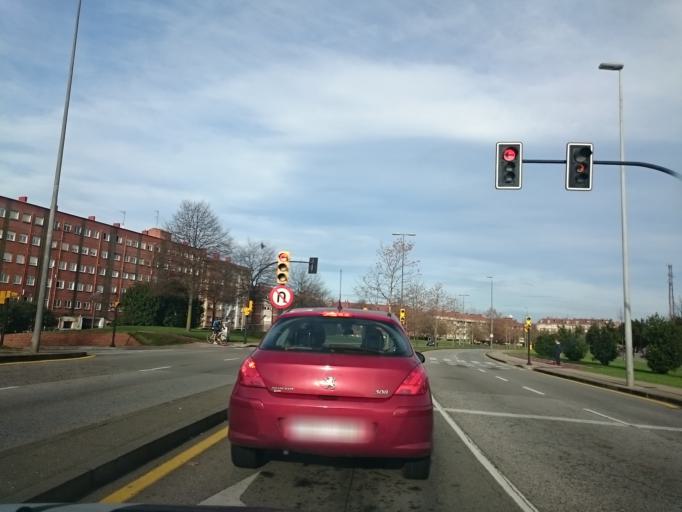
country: ES
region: Asturias
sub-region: Province of Asturias
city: Gijon
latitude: 43.5182
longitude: -5.6562
